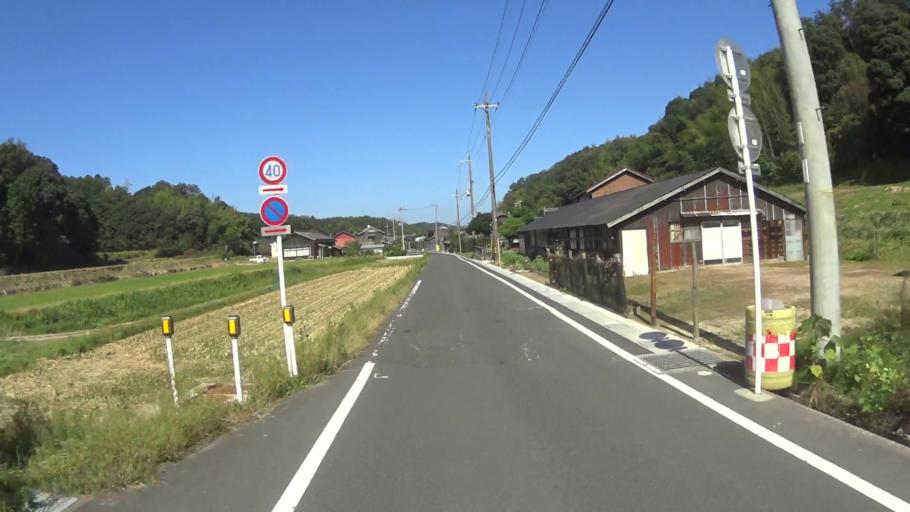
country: JP
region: Kyoto
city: Miyazu
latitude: 35.6753
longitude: 135.0549
